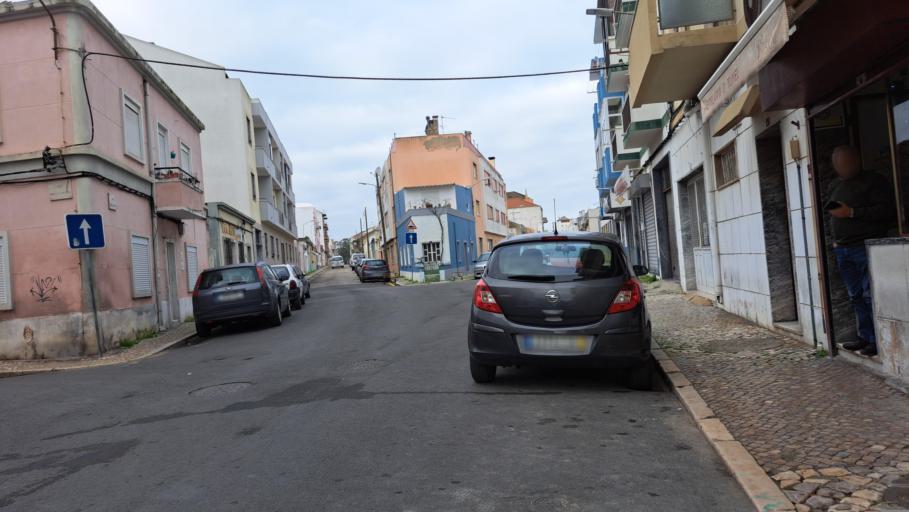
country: PT
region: Setubal
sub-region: Moita
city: Alhos Vedros
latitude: 38.6596
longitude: -9.0455
